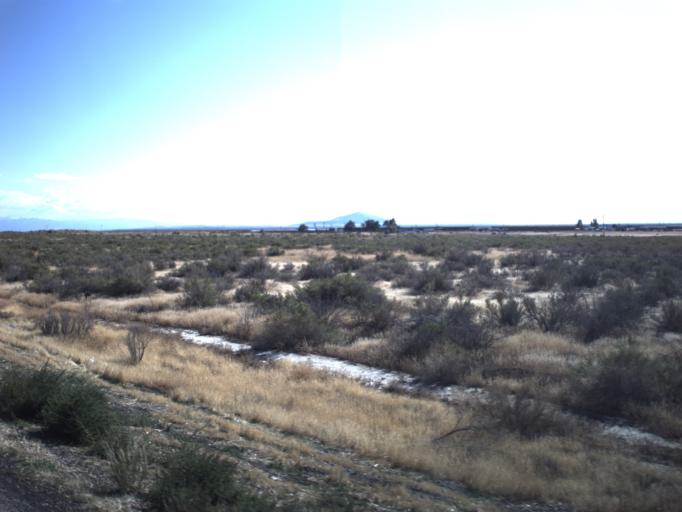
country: US
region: Utah
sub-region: Millard County
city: Delta
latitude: 39.3174
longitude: -112.4803
